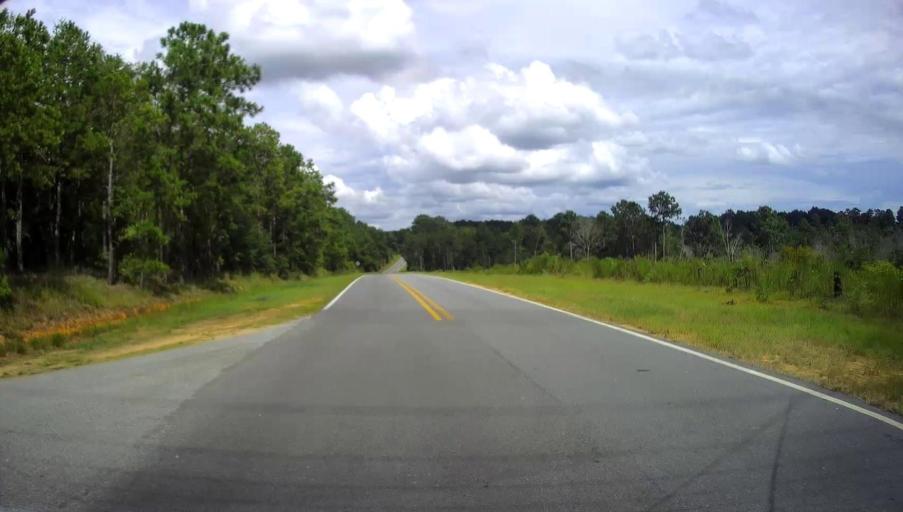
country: US
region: Georgia
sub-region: Chattahoochee County
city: Cusseta
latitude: 32.3074
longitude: -84.7600
